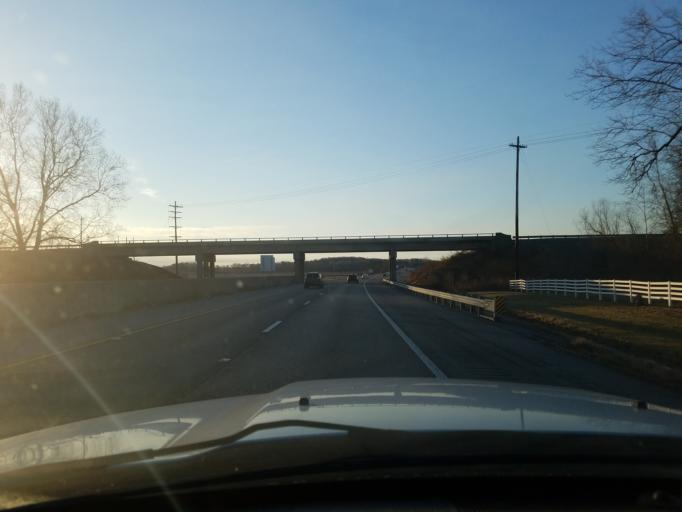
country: US
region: Kentucky
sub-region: Henderson County
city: Henderson
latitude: 37.8506
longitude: -87.5678
